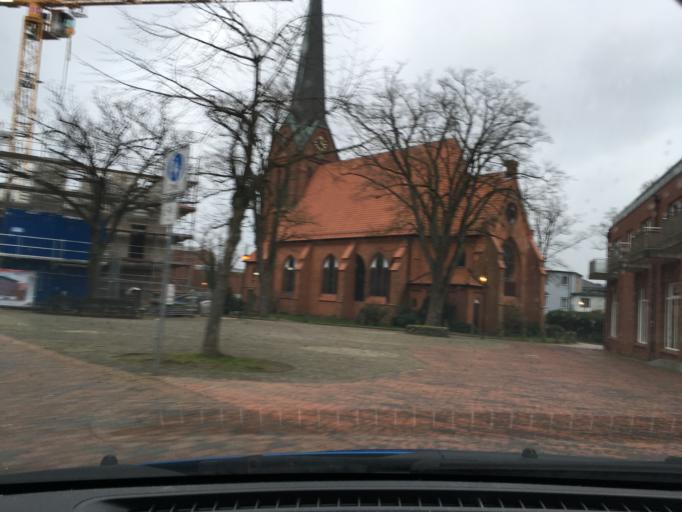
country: DE
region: Schleswig-Holstein
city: Schwarzenbek
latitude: 53.5022
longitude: 10.4799
